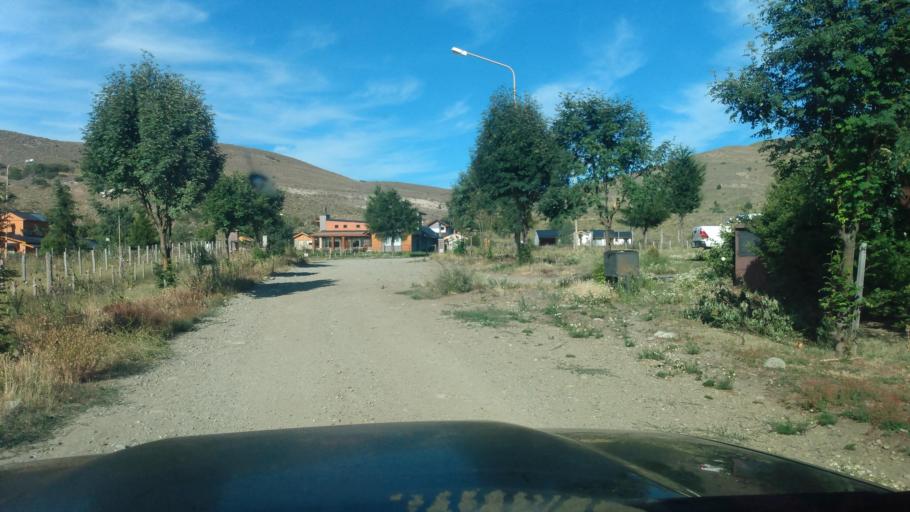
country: AR
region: Neuquen
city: Junin de los Andes
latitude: -39.9642
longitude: -71.0824
